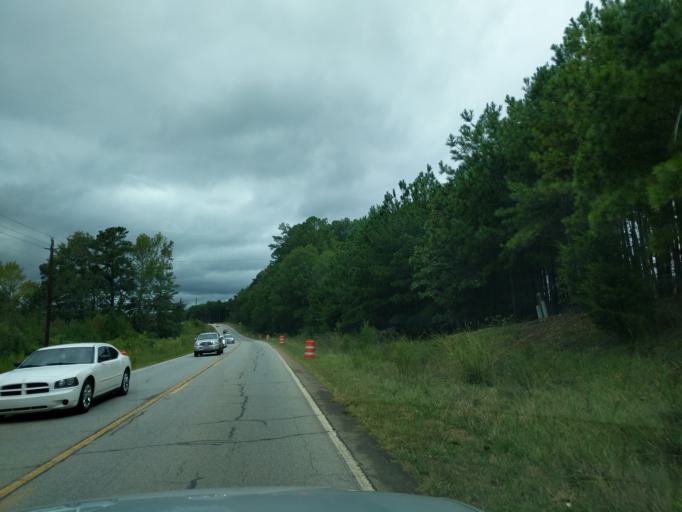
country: US
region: Georgia
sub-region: Wilkes County
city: Washington
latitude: 33.6844
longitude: -82.6403
